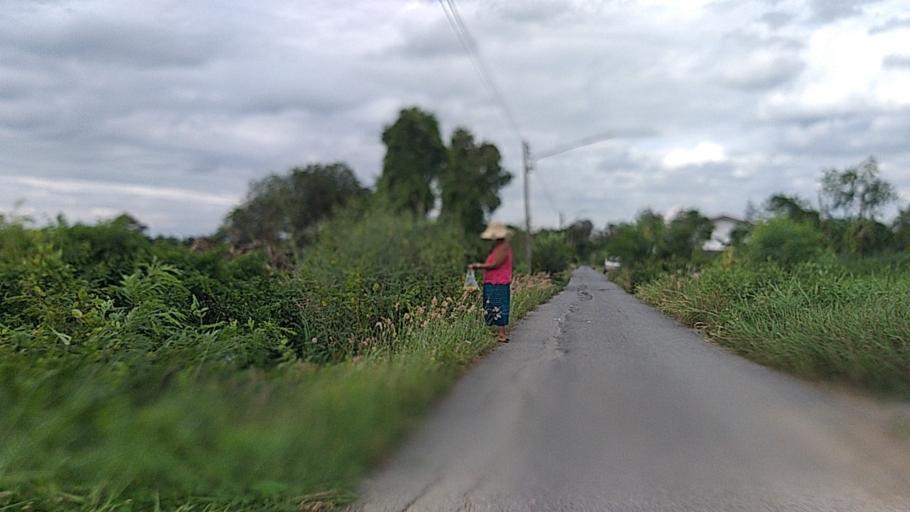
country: TH
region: Pathum Thani
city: Nong Suea
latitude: 14.0721
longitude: 100.8331
